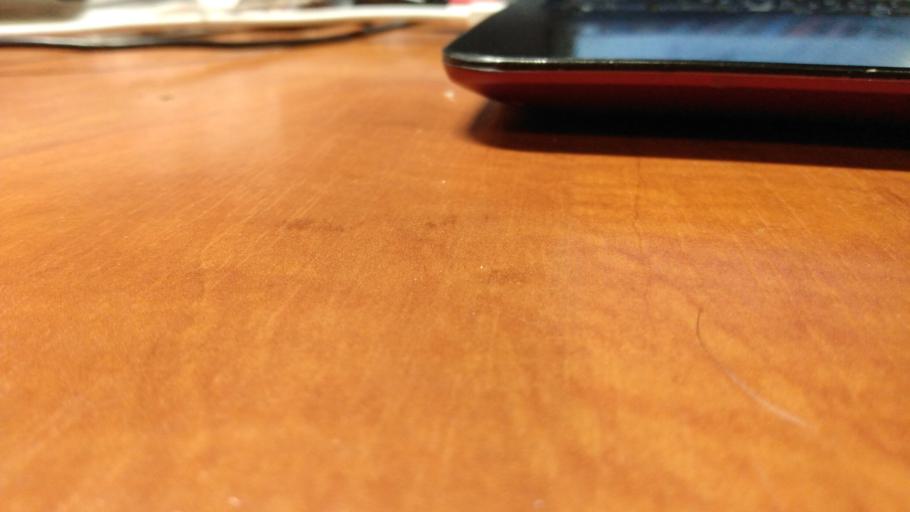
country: RU
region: Vologda
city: Babayevo
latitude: 59.1268
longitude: 36.1837
